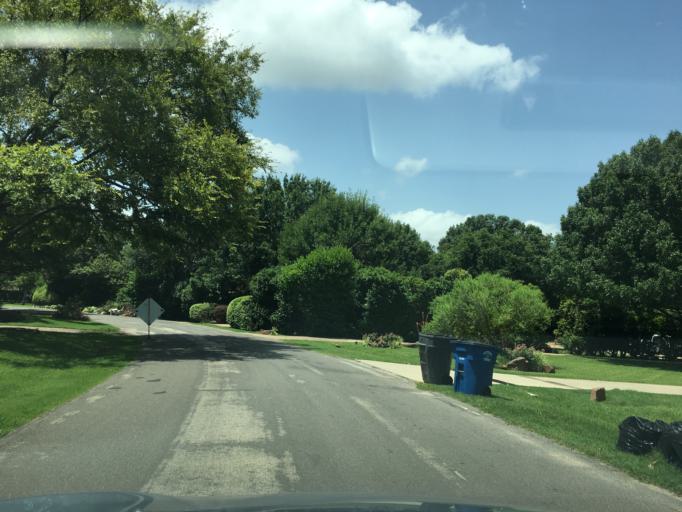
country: US
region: Texas
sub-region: Dallas County
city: University Park
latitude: 32.9052
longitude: -96.7957
